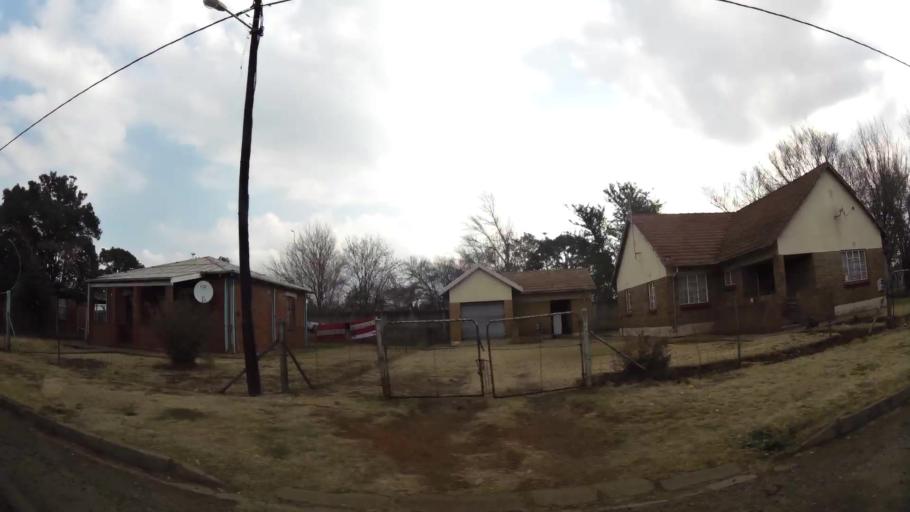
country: ZA
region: Gauteng
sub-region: Sedibeng District Municipality
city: Vereeniging
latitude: -26.6741
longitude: 27.9371
